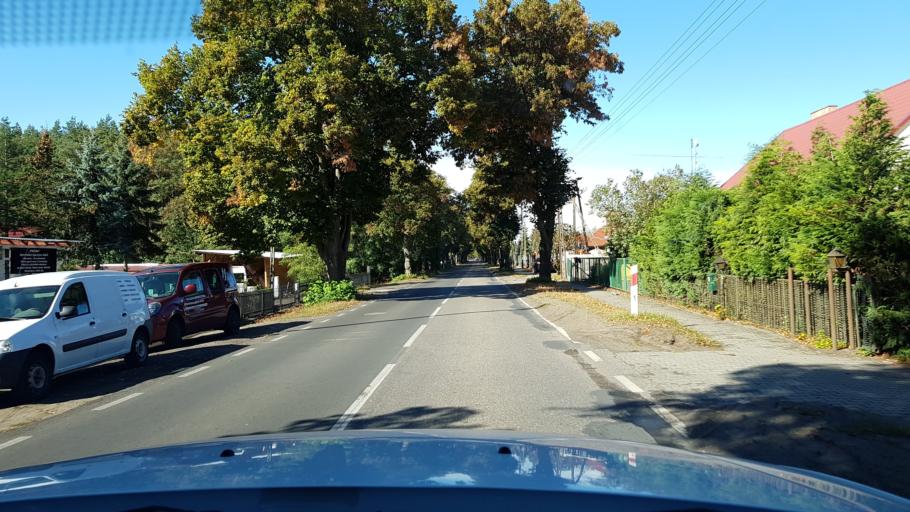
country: PL
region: West Pomeranian Voivodeship
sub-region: Powiat gryfinski
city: Gryfino
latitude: 53.2122
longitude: 14.4988
